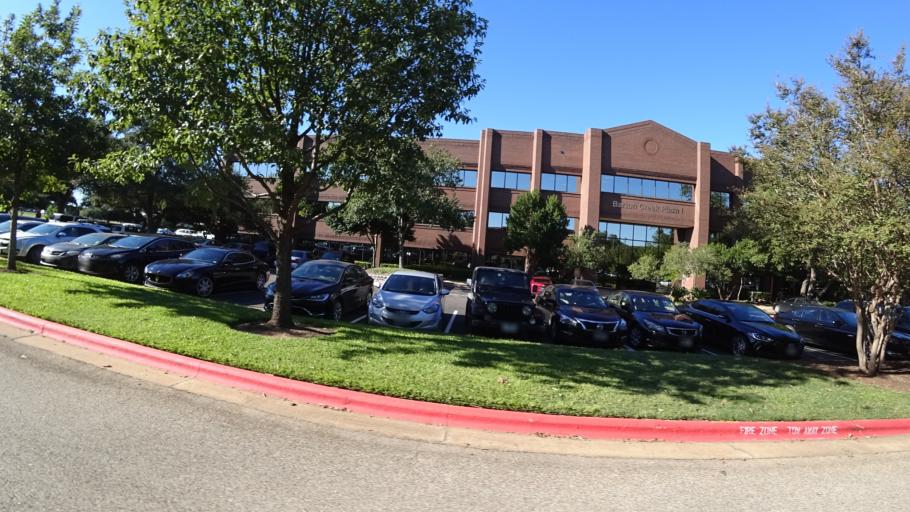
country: US
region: Texas
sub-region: Travis County
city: Rollingwood
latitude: 30.2428
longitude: -97.7998
